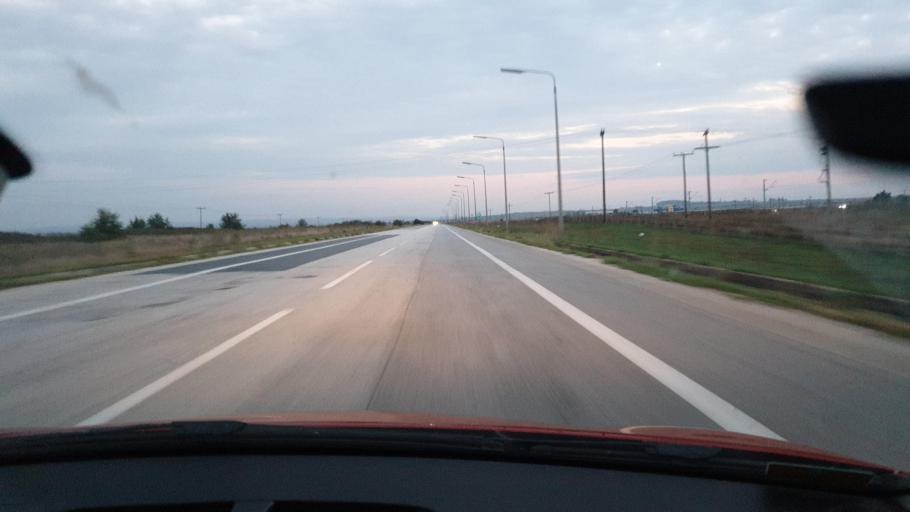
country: GR
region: Central Macedonia
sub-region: Nomos Kilkis
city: Agios Petros
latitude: 40.9147
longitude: 22.6502
